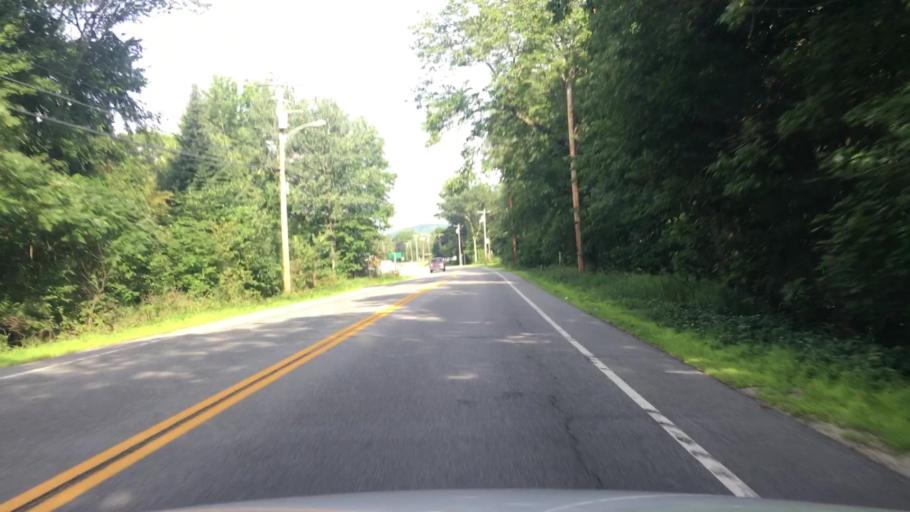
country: US
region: Maine
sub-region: Oxford County
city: Porter
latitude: 43.8049
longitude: -70.8706
